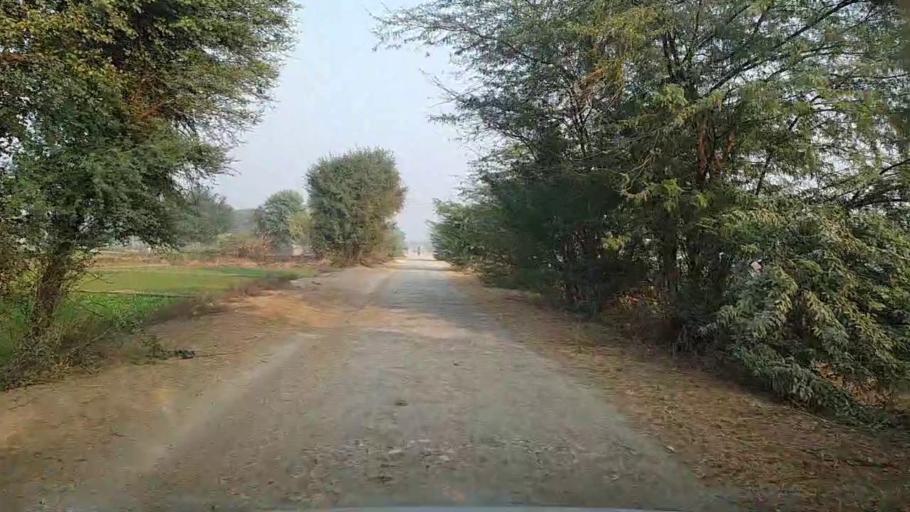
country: PK
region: Sindh
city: Bozdar
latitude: 27.0818
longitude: 68.5332
